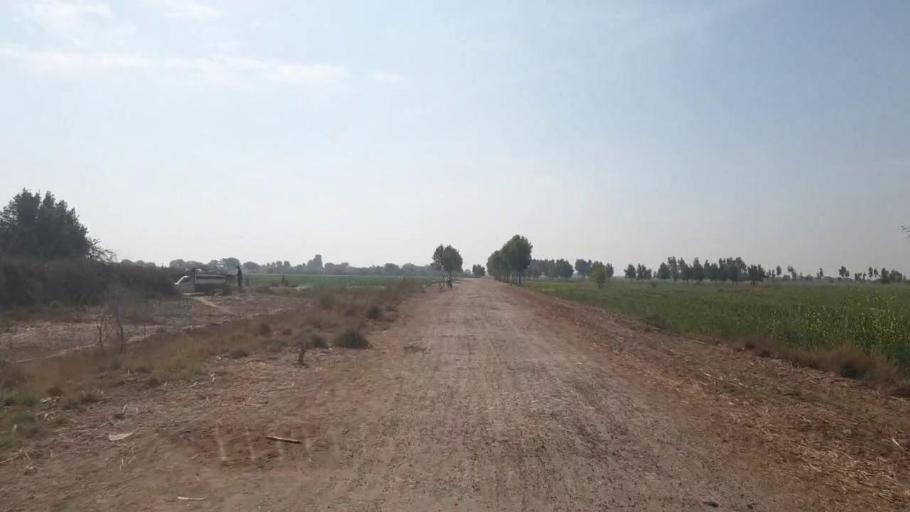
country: PK
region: Sindh
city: Mirwah Gorchani
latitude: 25.3721
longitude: 69.2031
